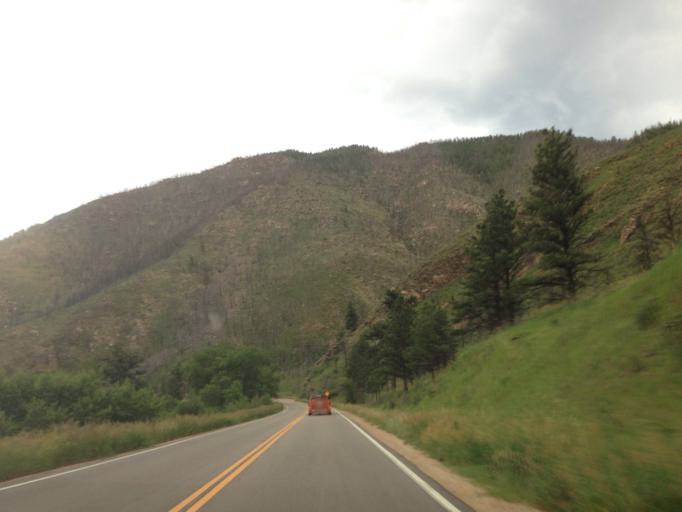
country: US
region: Colorado
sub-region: Larimer County
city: Laporte
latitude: 40.6842
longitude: -105.3858
